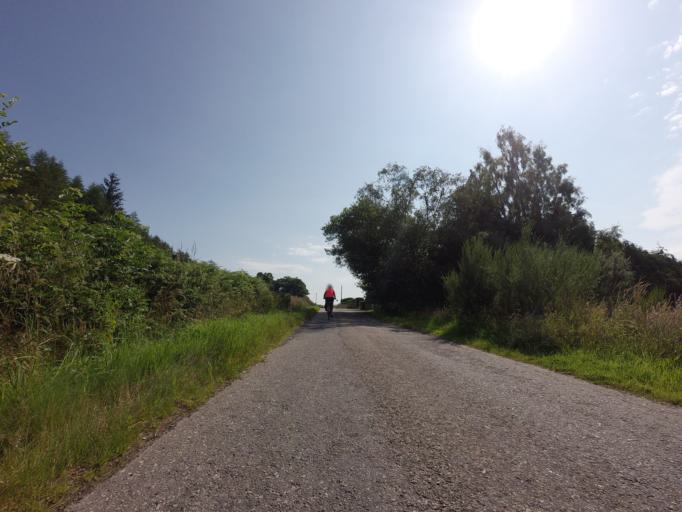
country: GB
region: Scotland
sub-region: Highland
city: Invergordon
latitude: 57.7586
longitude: -4.1275
